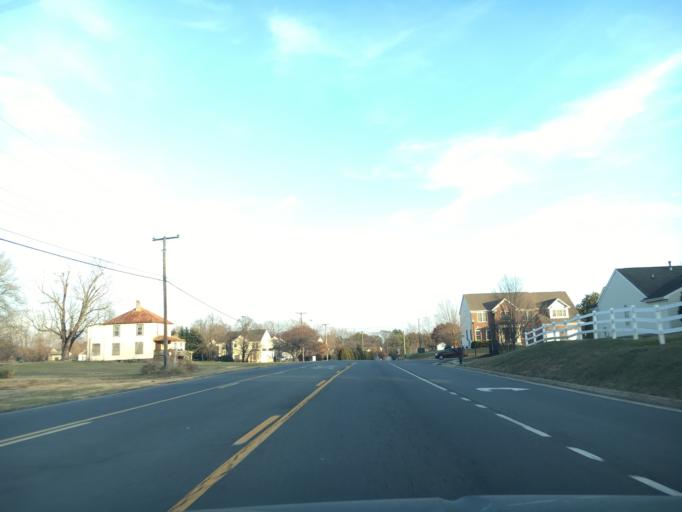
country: US
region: Virginia
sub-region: Culpeper County
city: Culpeper
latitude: 38.4827
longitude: -78.0127
